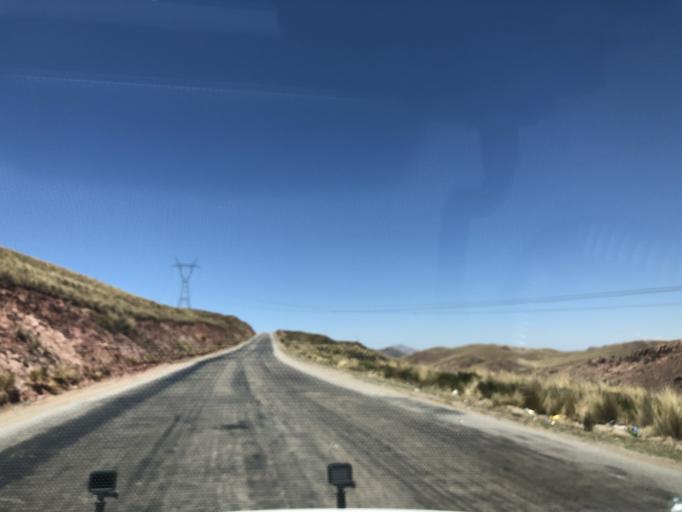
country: BO
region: Cochabamba
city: Colchani
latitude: -17.7002
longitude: -66.6956
